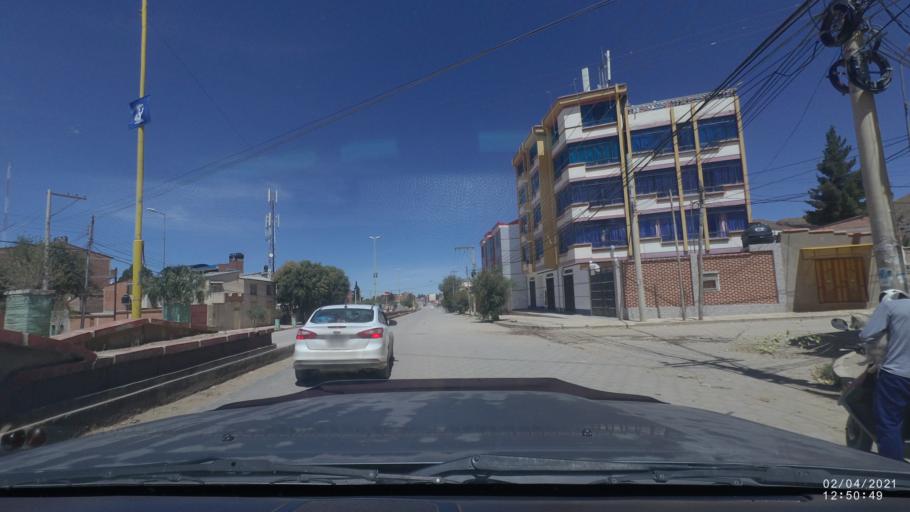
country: BO
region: Oruro
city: Oruro
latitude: -17.9780
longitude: -67.1375
